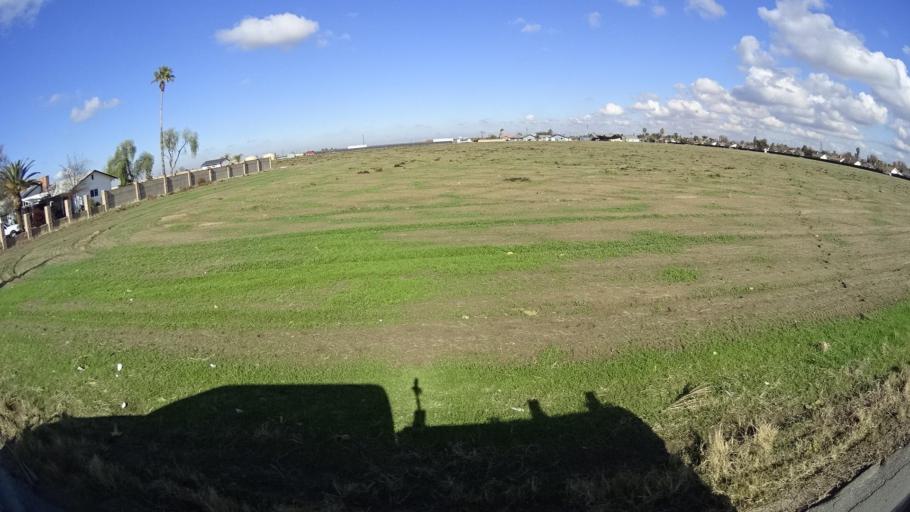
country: US
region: California
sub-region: Kern County
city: McFarland
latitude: 35.6741
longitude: -119.2428
